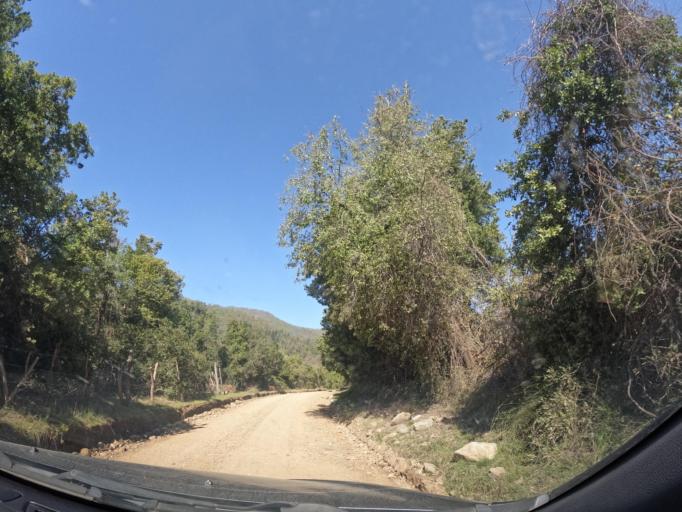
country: CL
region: Maule
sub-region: Provincia de Linares
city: Longavi
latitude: -36.2767
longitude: -71.4162
